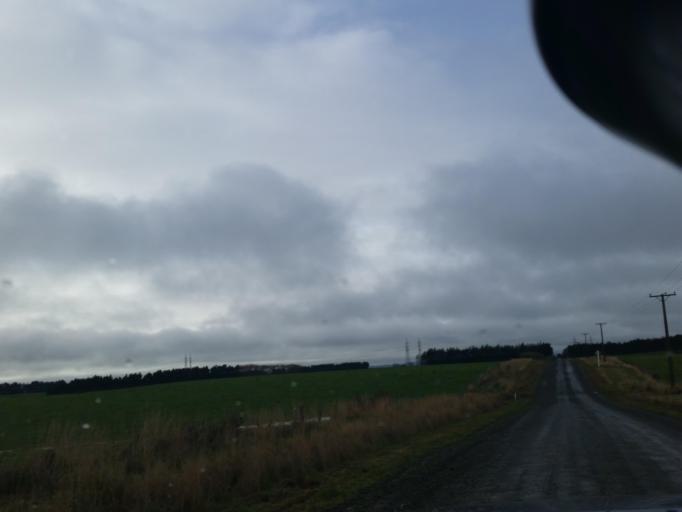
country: NZ
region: Southland
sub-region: Southland District
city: Winton
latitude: -46.2055
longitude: 168.1823
